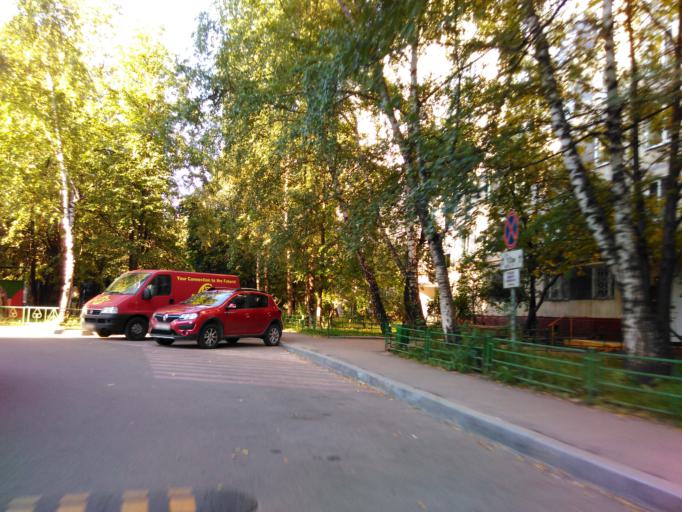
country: RU
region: Moscow
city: Tyoply Stan
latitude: 55.6285
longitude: 37.5063
